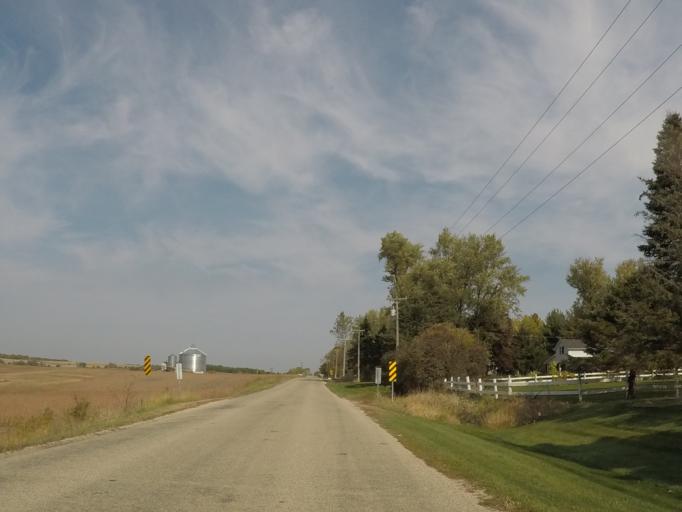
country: US
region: Wisconsin
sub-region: Dane County
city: Cross Plains
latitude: 43.0556
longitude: -89.6009
